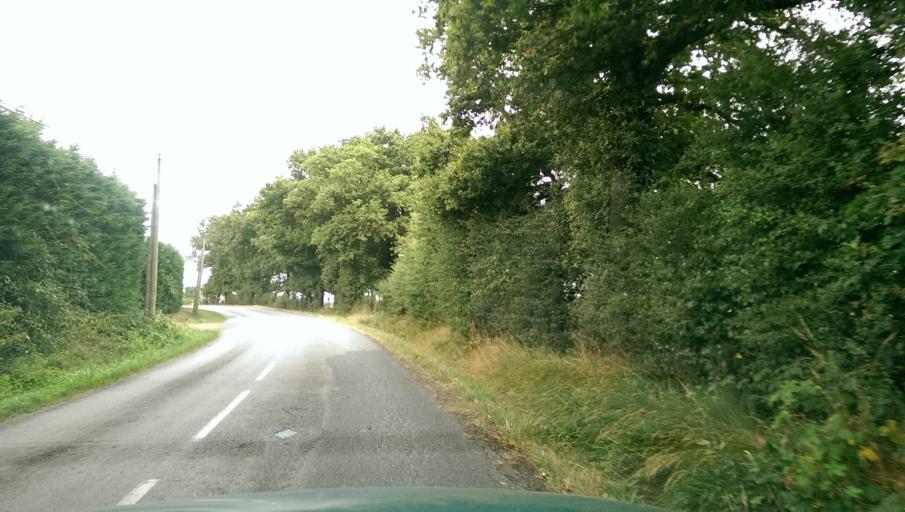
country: FR
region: Pays de la Loire
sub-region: Departement de la Loire-Atlantique
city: Remouille
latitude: 47.0451
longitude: -1.3916
